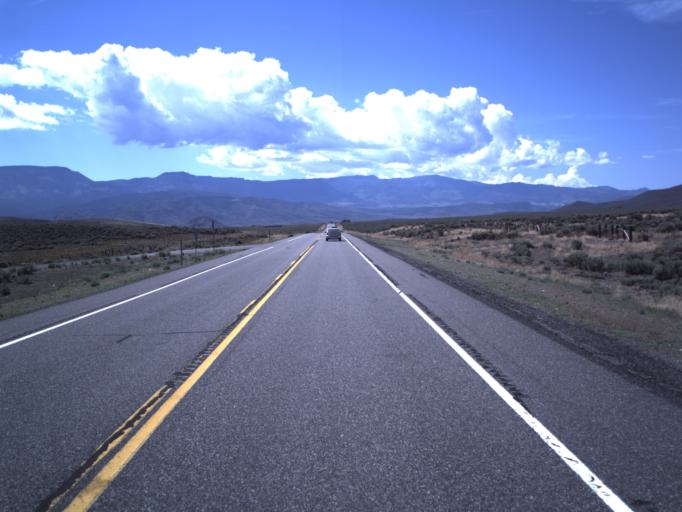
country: US
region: Utah
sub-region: Piute County
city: Junction
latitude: 38.2770
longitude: -112.2237
